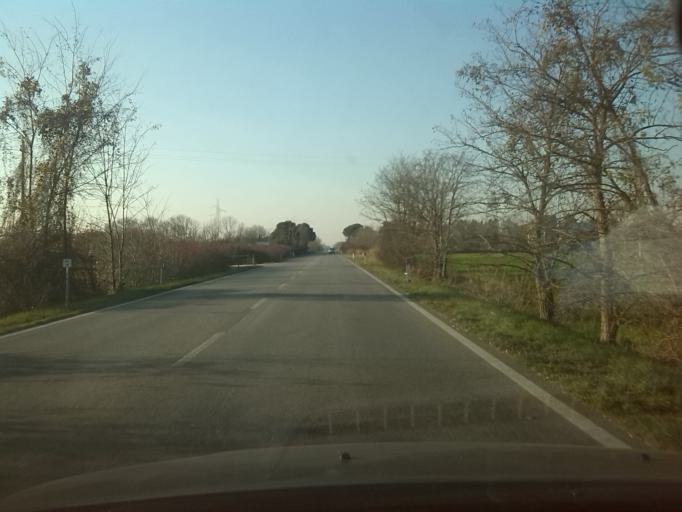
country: IT
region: Friuli Venezia Giulia
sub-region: Provincia di Udine
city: Castions di Strada
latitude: 45.9187
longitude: 13.1953
